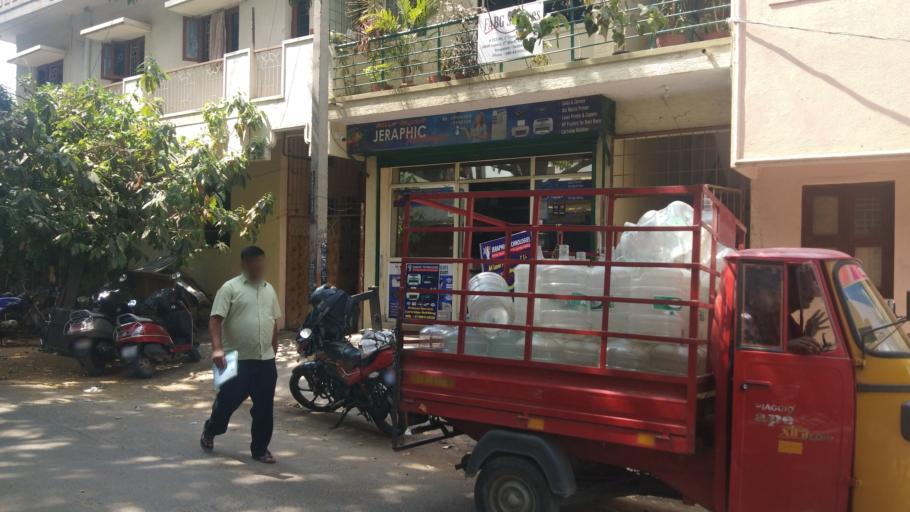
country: IN
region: Karnataka
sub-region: Bangalore Urban
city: Bangalore
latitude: 13.0172
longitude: 77.6401
